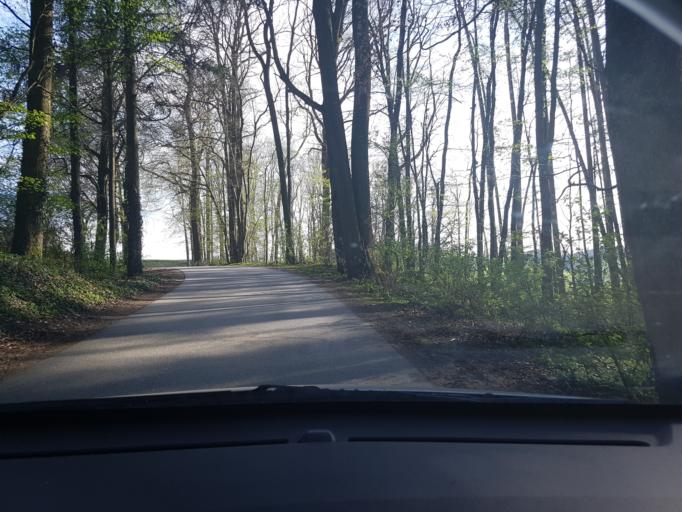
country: AT
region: Upper Austria
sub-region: Politischer Bezirk Linz-Land
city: Ansfelden
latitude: 48.1737
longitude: 14.3298
